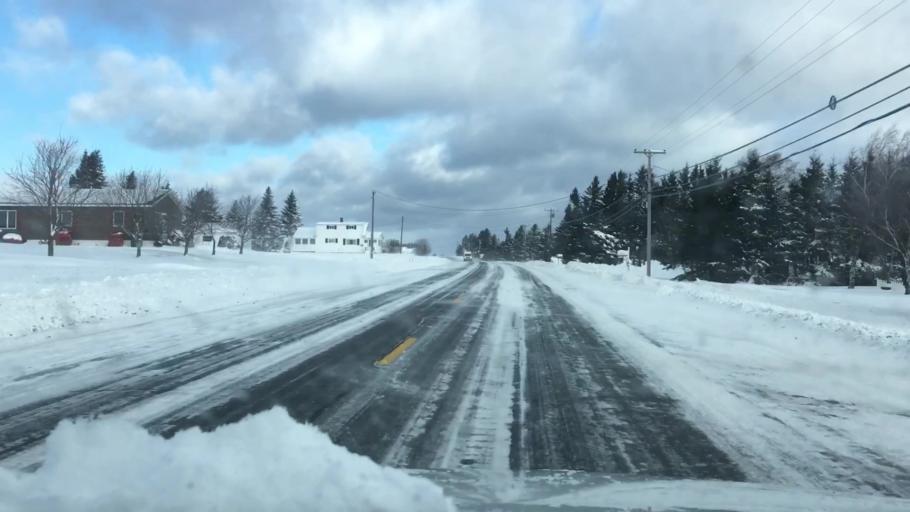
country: US
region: Maine
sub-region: Aroostook County
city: Caribou
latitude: 46.9052
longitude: -68.0158
